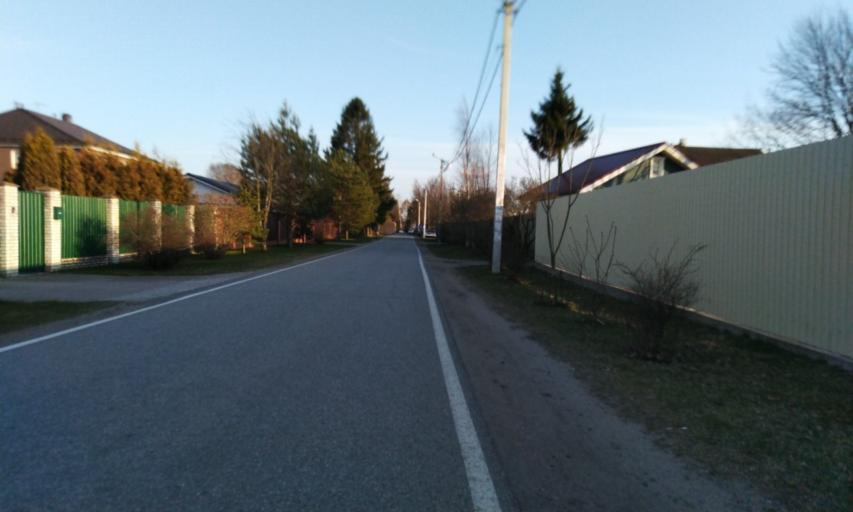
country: RU
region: Leningrad
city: Novoye Devyatkino
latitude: 60.0987
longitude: 30.4487
